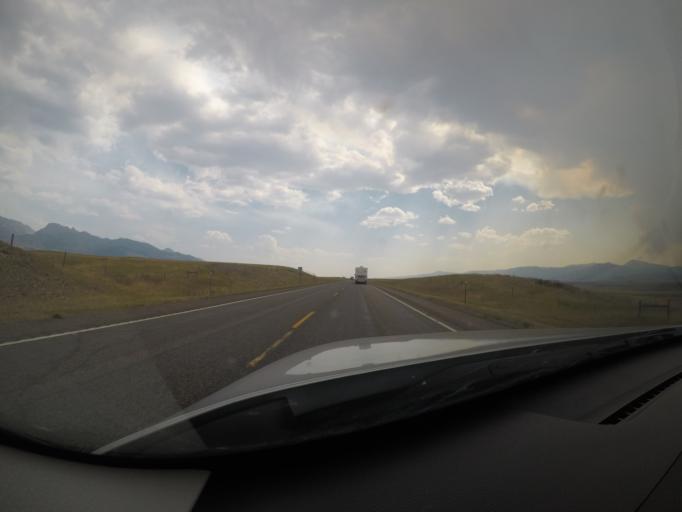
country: US
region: Montana
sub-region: Gallatin County
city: Big Sky
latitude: 45.0922
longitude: -111.6481
